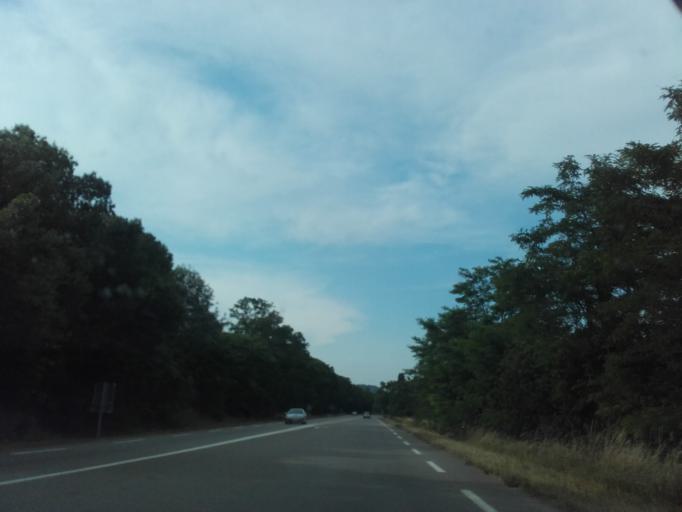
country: FR
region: Rhone-Alpes
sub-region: Departement de l'Ardeche
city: Charmes-sur-Rhone
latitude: 44.8544
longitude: 4.8530
